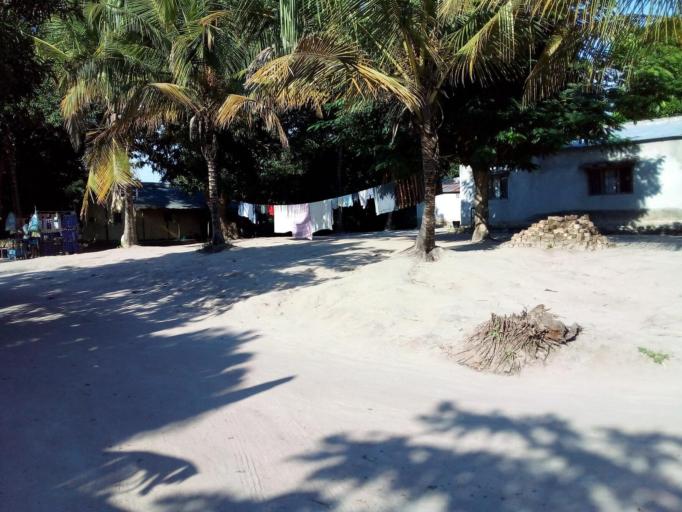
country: MZ
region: Zambezia
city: Quelimane
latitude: -17.5975
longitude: 36.8059
